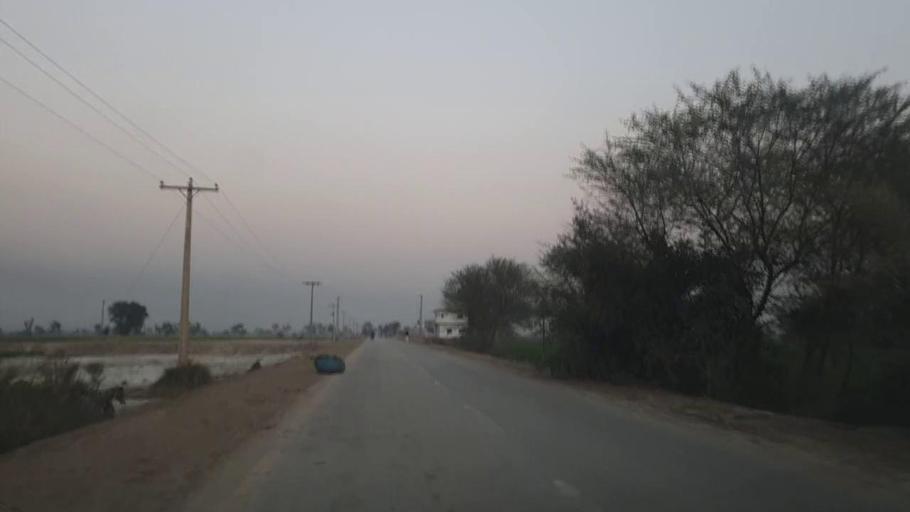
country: PK
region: Sindh
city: Naushahro Firoz
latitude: 26.8491
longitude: 68.0485
